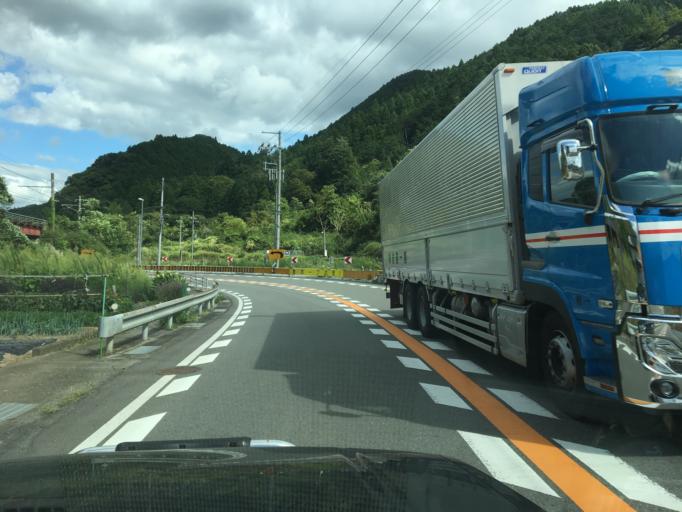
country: JP
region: Kyoto
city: Fukuchiyama
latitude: 35.3175
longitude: 134.8892
